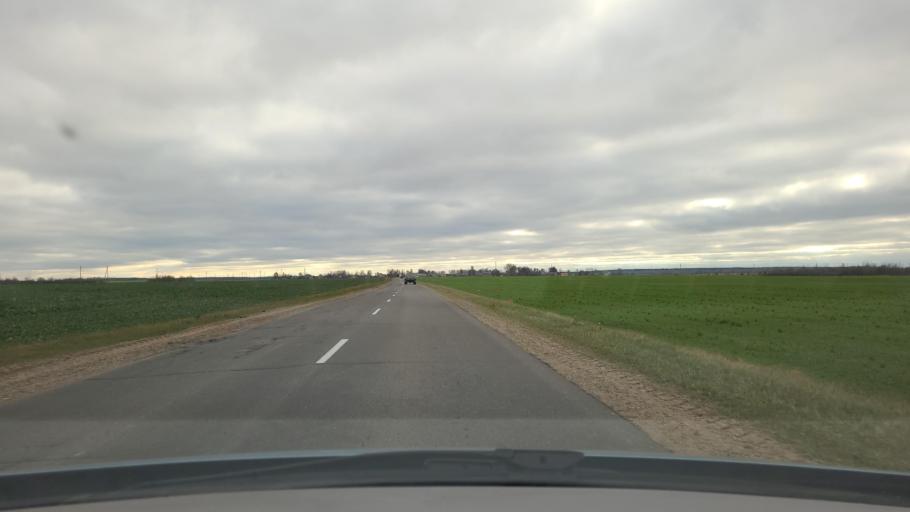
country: BY
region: Minsk
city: Krupki
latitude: 54.3821
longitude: 29.0523
